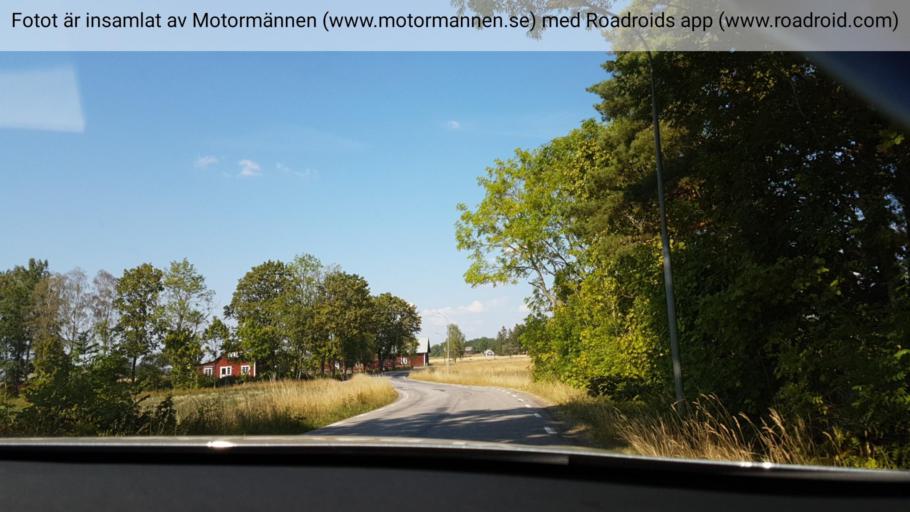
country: SE
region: Vaestra Goetaland
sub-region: Mariestads Kommun
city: Mariestad
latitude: 58.6020
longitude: 13.8668
